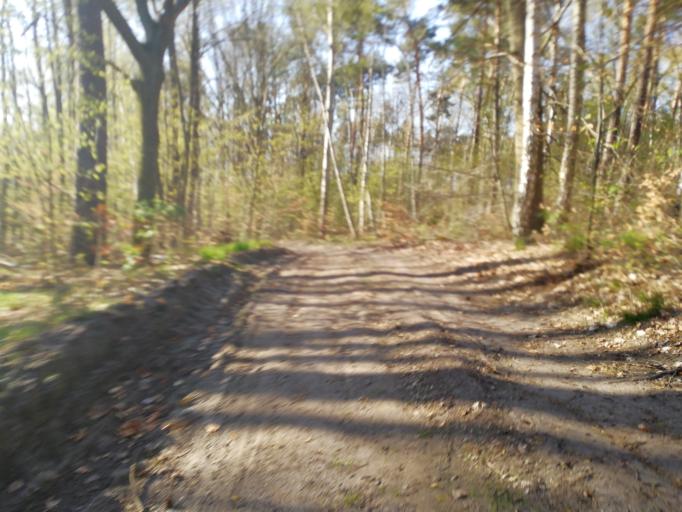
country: DE
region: Brandenburg
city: Calau
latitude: 51.7197
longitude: 13.9588
